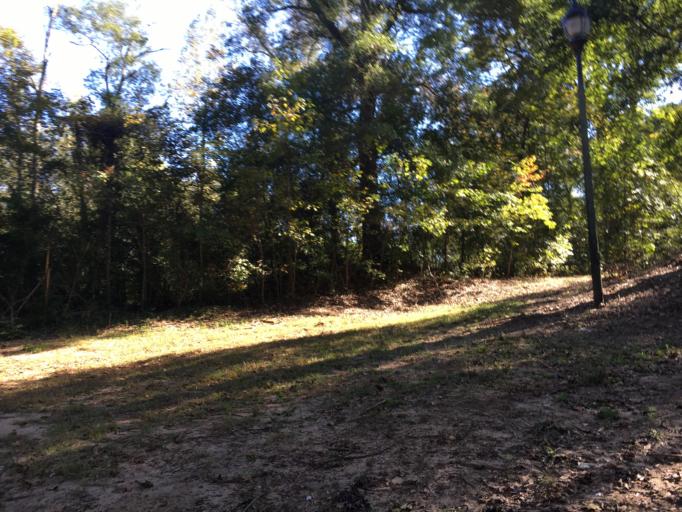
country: US
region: South Carolina
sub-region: Spartanburg County
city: Lyman
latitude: 34.9400
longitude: -82.1221
